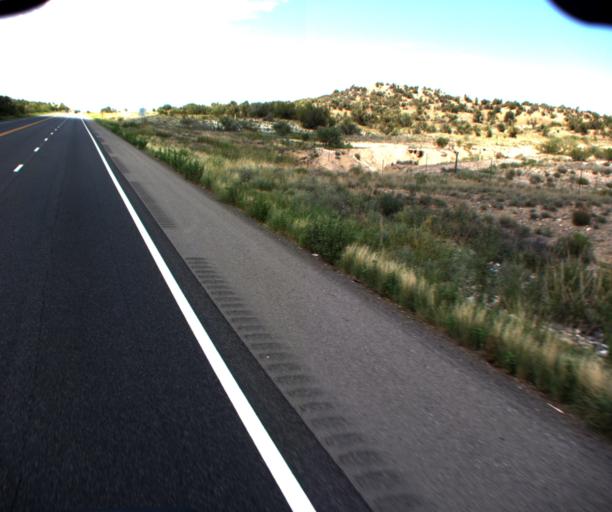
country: US
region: Arizona
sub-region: Yavapai County
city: Cornville
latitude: 34.6419
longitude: -111.9477
